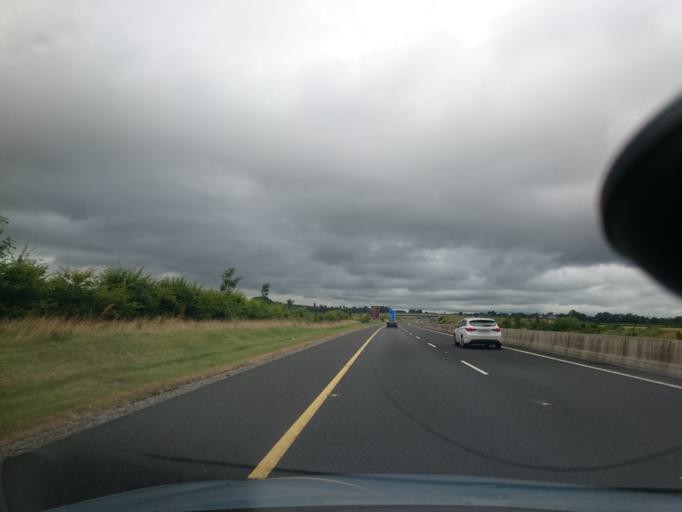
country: IE
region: Leinster
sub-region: Kildare
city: Moone
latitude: 52.9832
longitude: -6.8533
